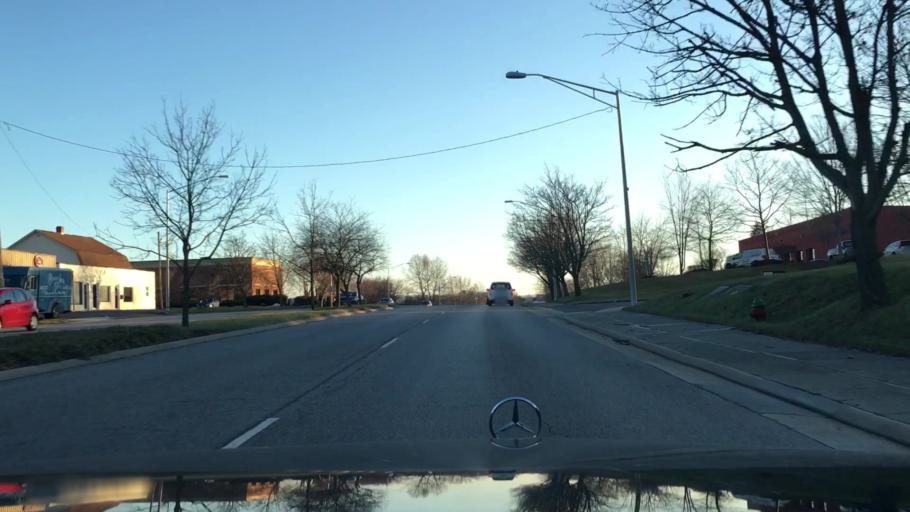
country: US
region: Virginia
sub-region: Montgomery County
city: Blacksburg
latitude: 37.2085
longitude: -80.3992
